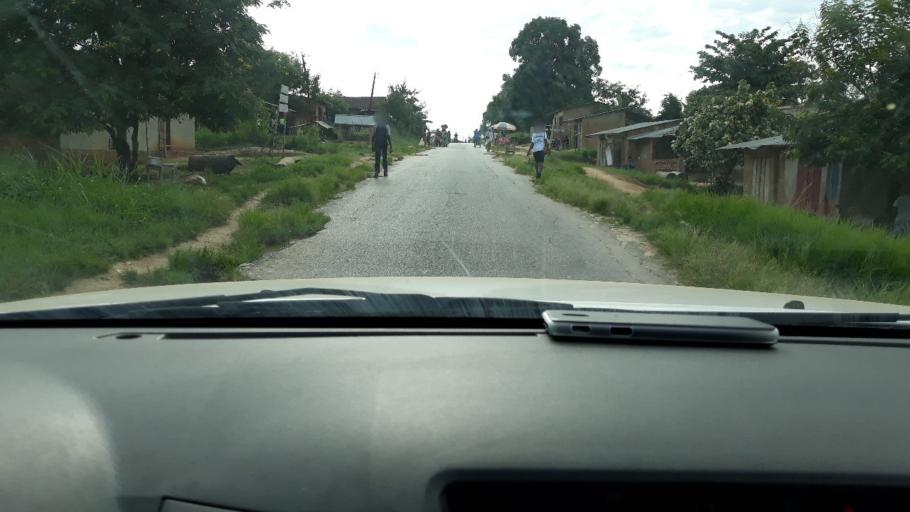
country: CD
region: Maniema
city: Kindu
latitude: -2.9515
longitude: 25.9459
